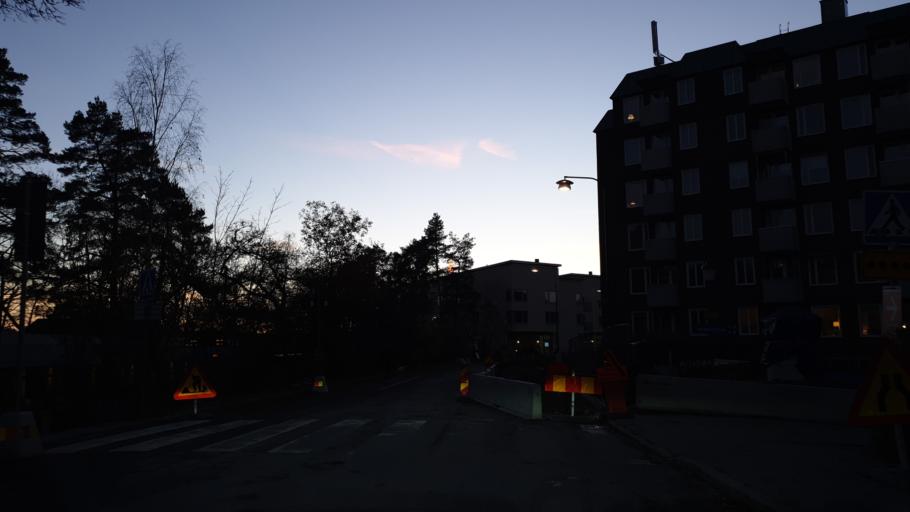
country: SE
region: Stockholm
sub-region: Stockholms Kommun
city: Bromma
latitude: 59.3299
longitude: 17.9211
